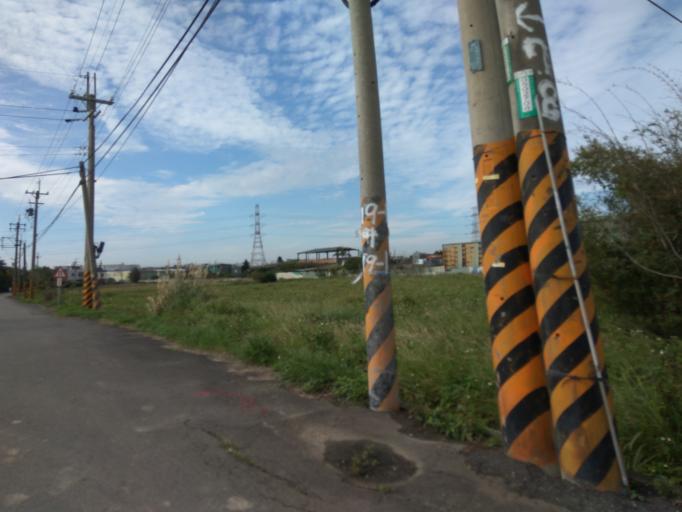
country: TW
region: Taiwan
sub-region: Hsinchu
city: Zhubei
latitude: 24.9500
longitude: 121.1098
